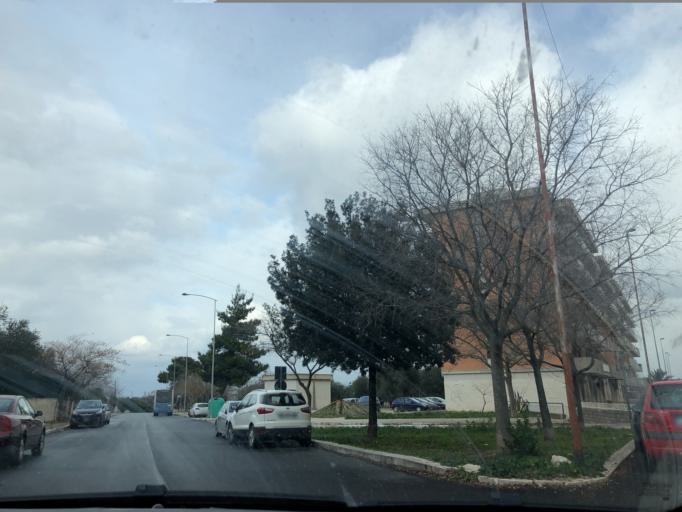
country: IT
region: Apulia
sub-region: Provincia di Foggia
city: Lucera
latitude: 41.5005
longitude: 15.3532
